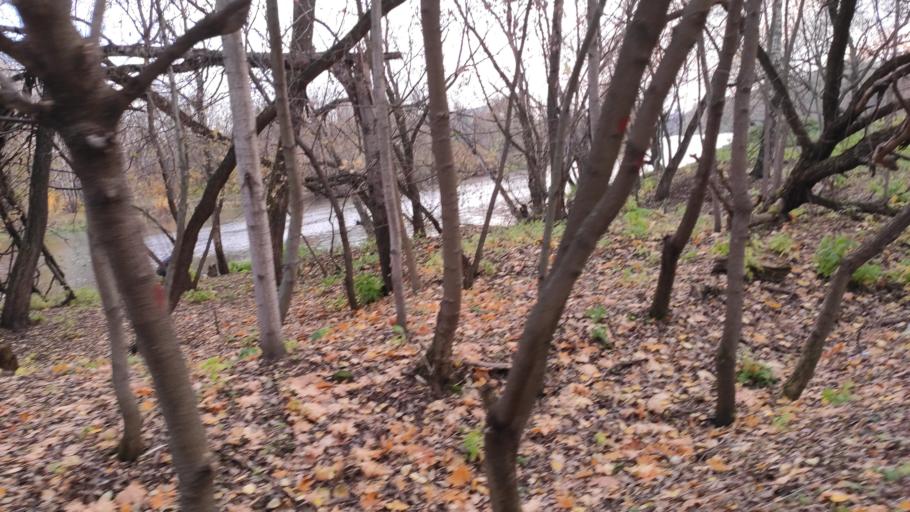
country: RU
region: Moskovskaya
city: Noginsk
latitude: 55.8687
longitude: 38.4525
